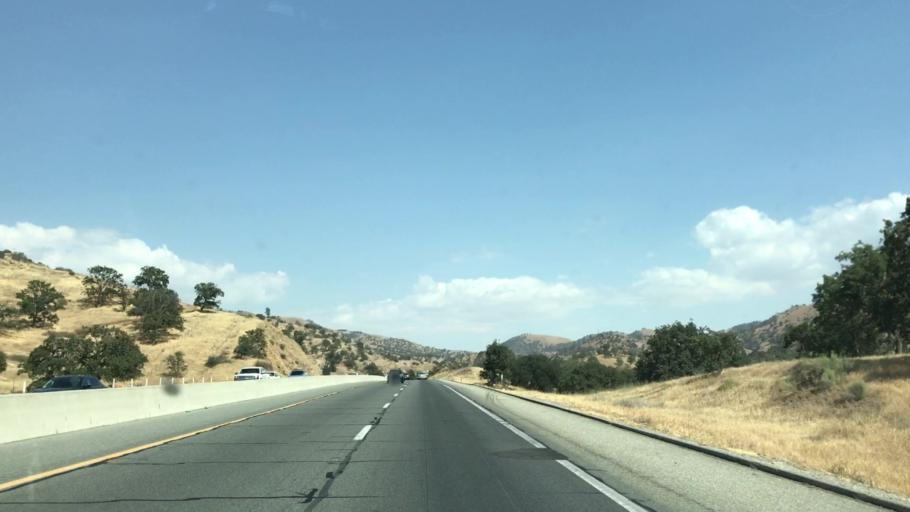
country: US
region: California
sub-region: Kern County
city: Golden Hills
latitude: 35.2101
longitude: -118.5425
